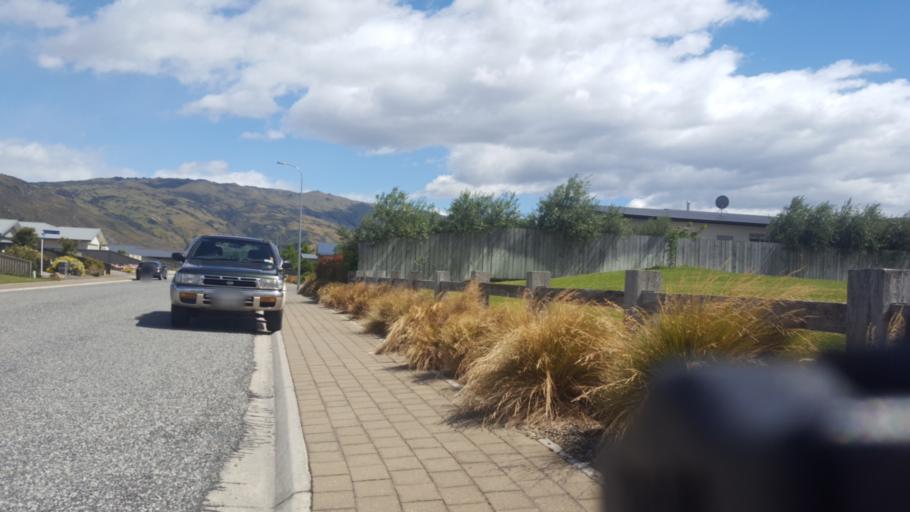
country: NZ
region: Otago
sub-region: Queenstown-Lakes District
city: Wanaka
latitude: -45.1960
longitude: 169.3328
